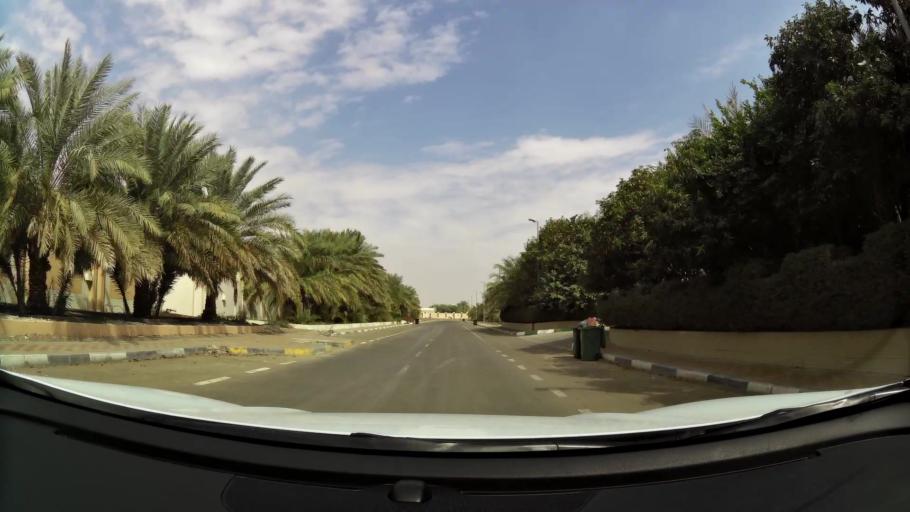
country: AE
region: Abu Dhabi
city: Al Ain
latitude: 24.1918
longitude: 55.7993
